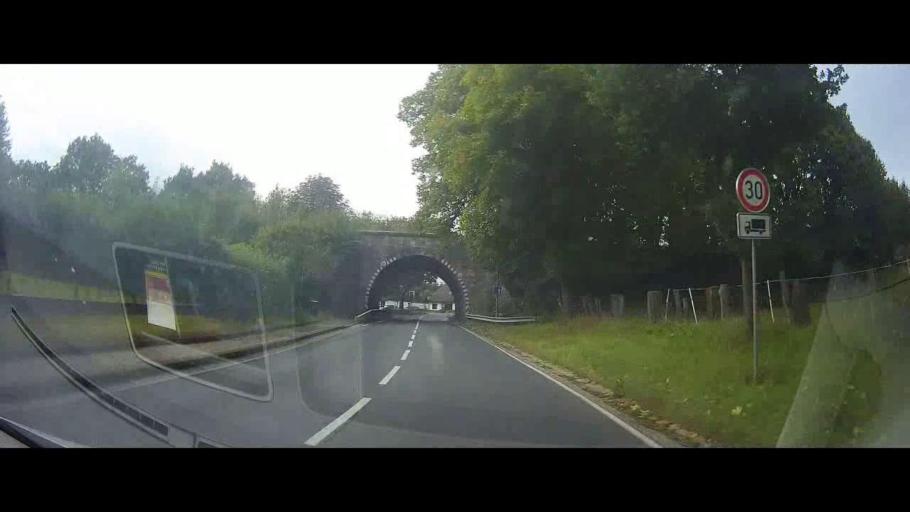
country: DE
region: Lower Saxony
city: Uslar
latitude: 51.6257
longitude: 9.6621
